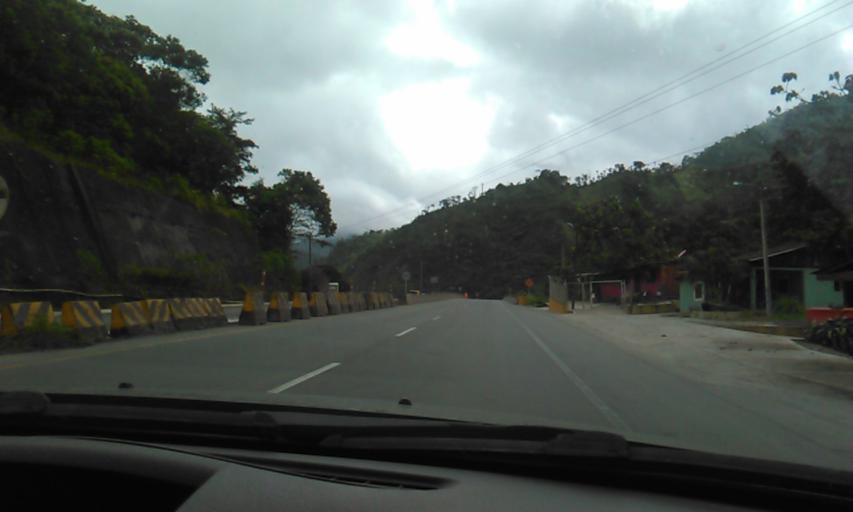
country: CO
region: Valle del Cauca
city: Dagua
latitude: 3.8078
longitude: -76.7774
